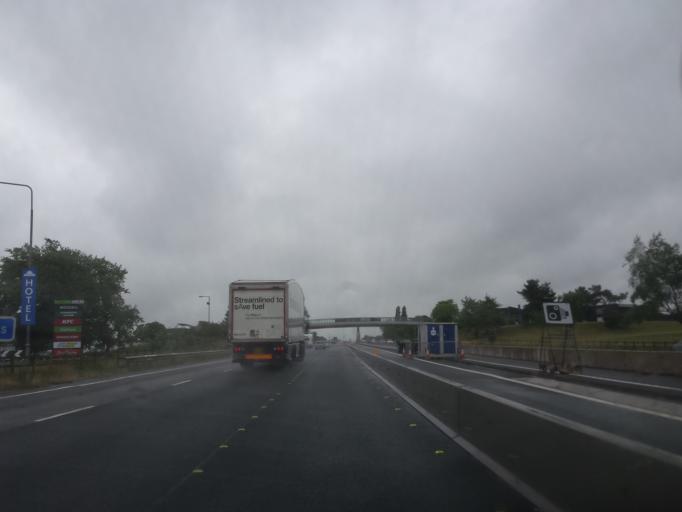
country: GB
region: England
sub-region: Rotherham
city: Harthill
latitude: 53.3174
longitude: -1.2814
